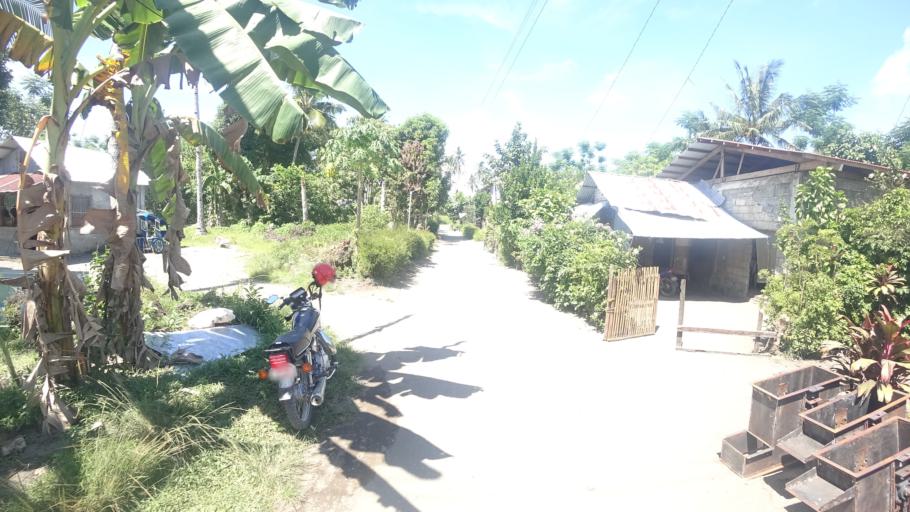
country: PH
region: Eastern Visayas
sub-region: Province of Leyte
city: Mayorga
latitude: 10.8886
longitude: 125.0089
